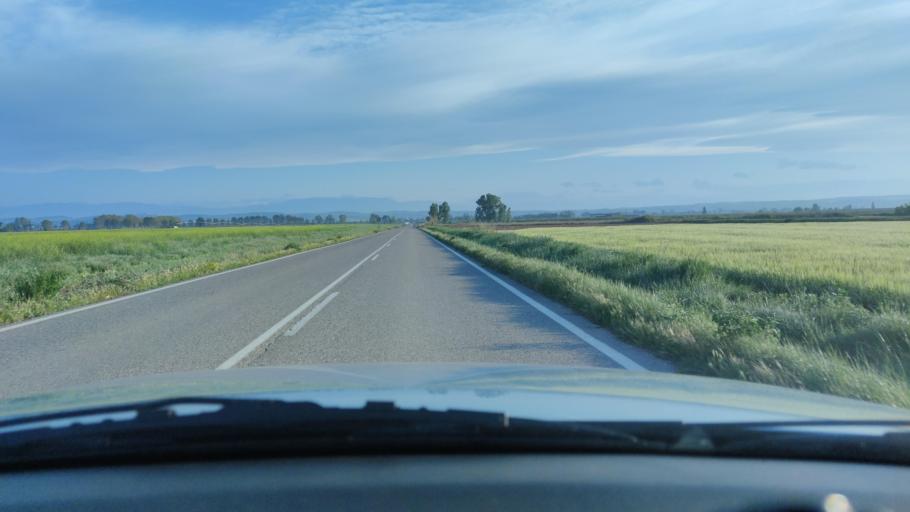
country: ES
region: Catalonia
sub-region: Provincia de Lleida
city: Ivars d'Urgell
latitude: 41.7114
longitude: 0.9823
